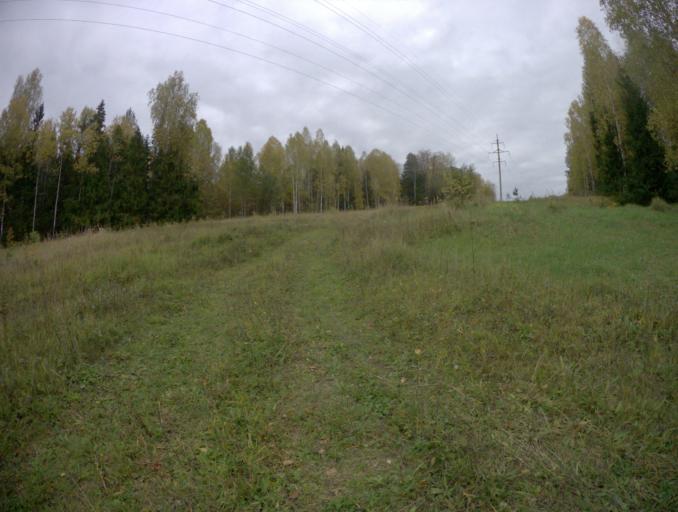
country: RU
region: Vladimir
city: Stepantsevo
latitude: 56.3075
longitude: 41.7411
